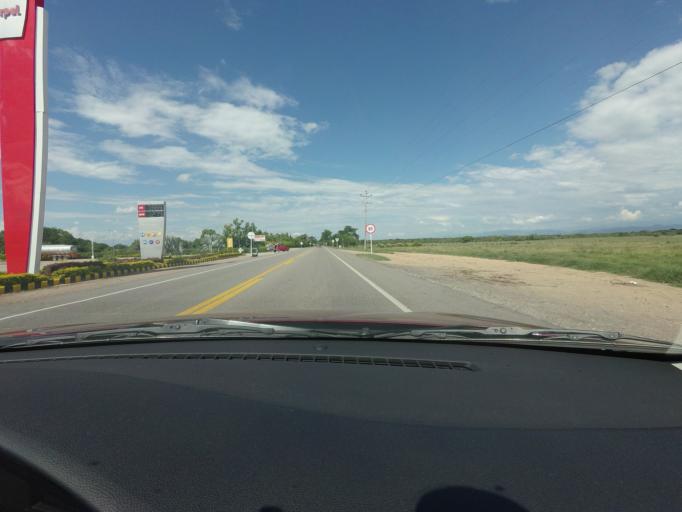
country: CO
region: Tolima
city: Natagaima
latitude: 3.6393
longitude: -75.0918
